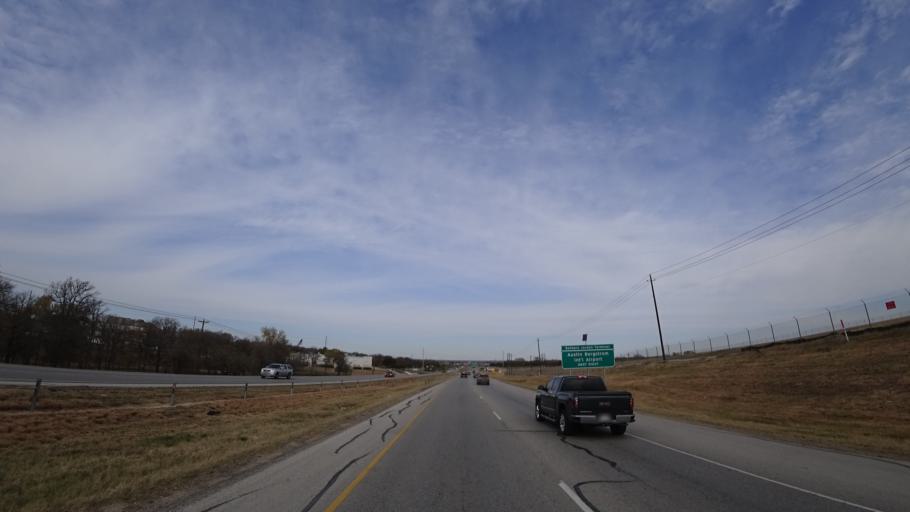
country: US
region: Texas
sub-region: Travis County
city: Austin
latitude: 30.2139
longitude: -97.6832
